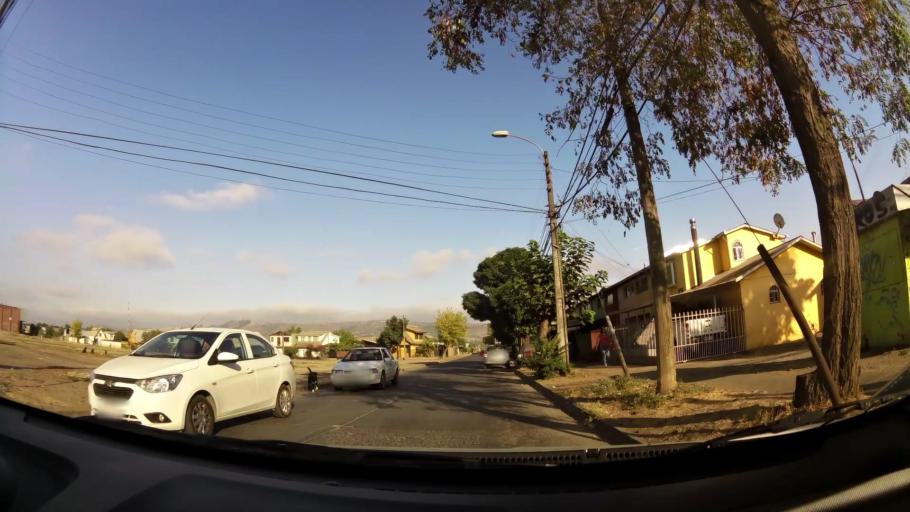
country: CL
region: Maule
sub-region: Provincia de Talca
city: Talca
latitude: -35.4108
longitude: -71.6503
